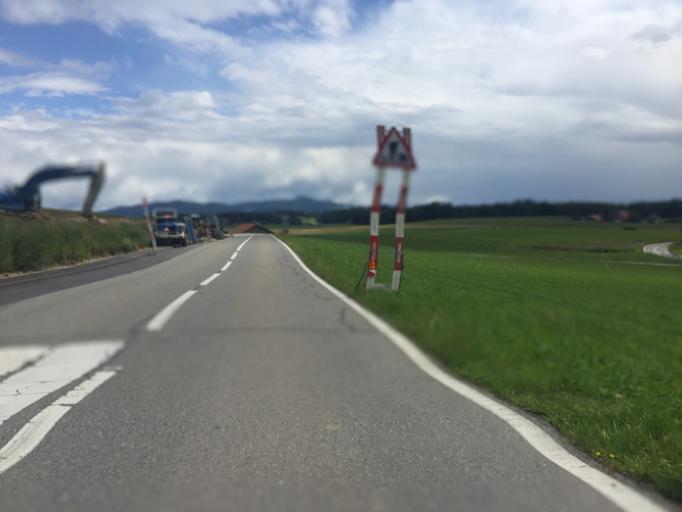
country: CH
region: Bern
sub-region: Bern-Mittelland District
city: Kirchlindach
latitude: 46.9877
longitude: 7.3910
